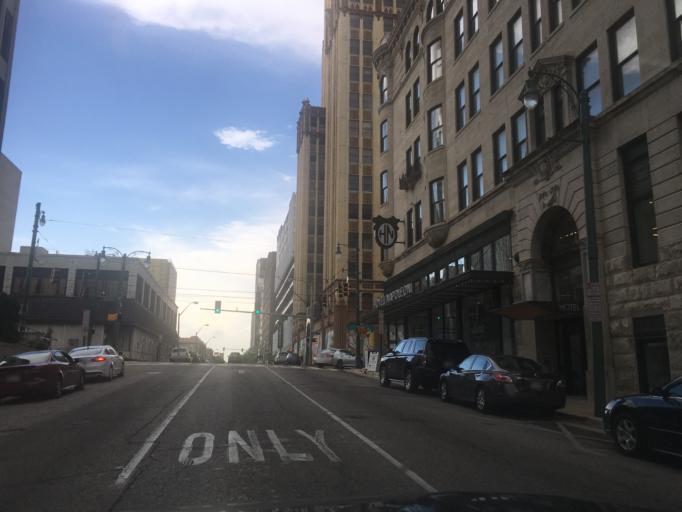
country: US
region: Tennessee
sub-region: Shelby County
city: Memphis
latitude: 35.1440
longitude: -90.0505
